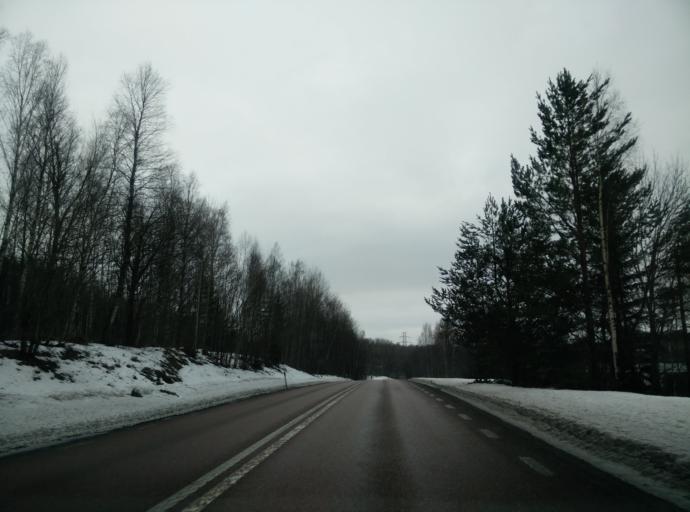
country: SE
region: Gaevleborg
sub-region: Hofors Kommun
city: Hofors
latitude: 60.5510
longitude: 16.3133
